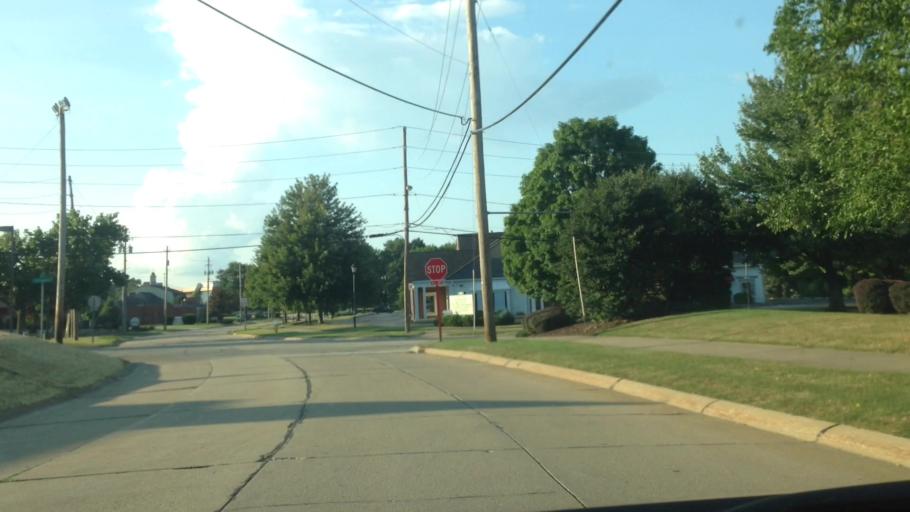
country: US
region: Ohio
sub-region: Summit County
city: Fairlawn
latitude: 41.1310
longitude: -81.6127
